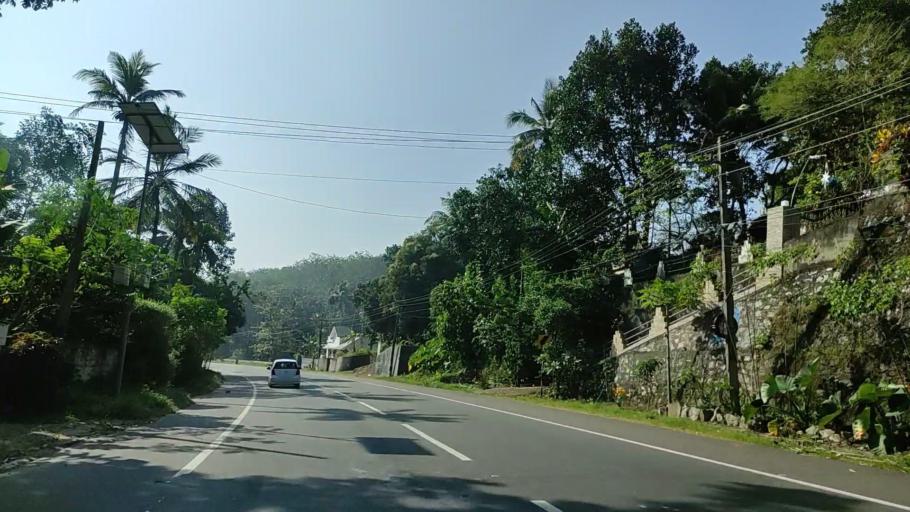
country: IN
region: Kerala
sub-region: Kollam
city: Punalur
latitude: 8.9136
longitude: 76.8533
